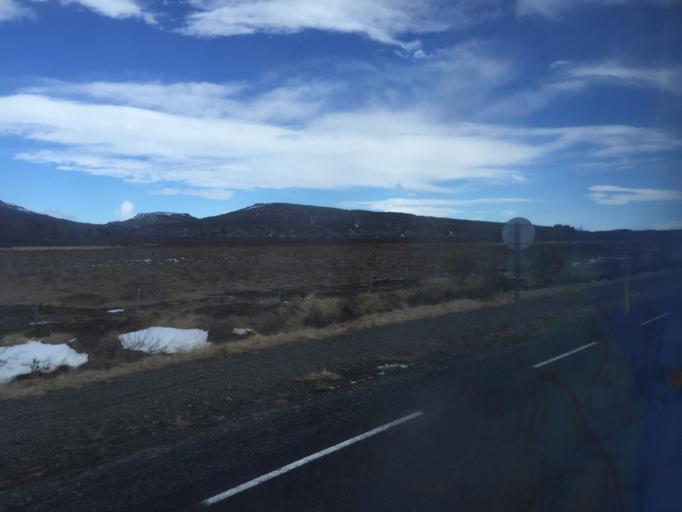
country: IS
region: South
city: Selfoss
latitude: 64.2255
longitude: -20.5970
